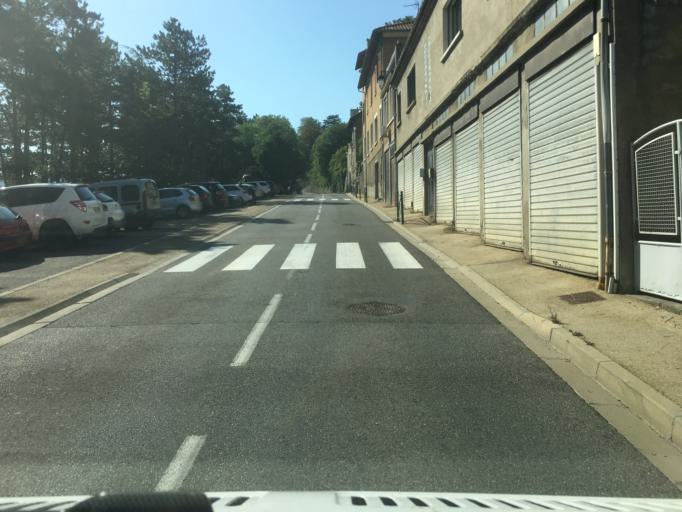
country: FR
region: Provence-Alpes-Cote d'Azur
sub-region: Departement des Alpes-de-Haute-Provence
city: Sisteron
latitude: 44.1935
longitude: 5.9421
